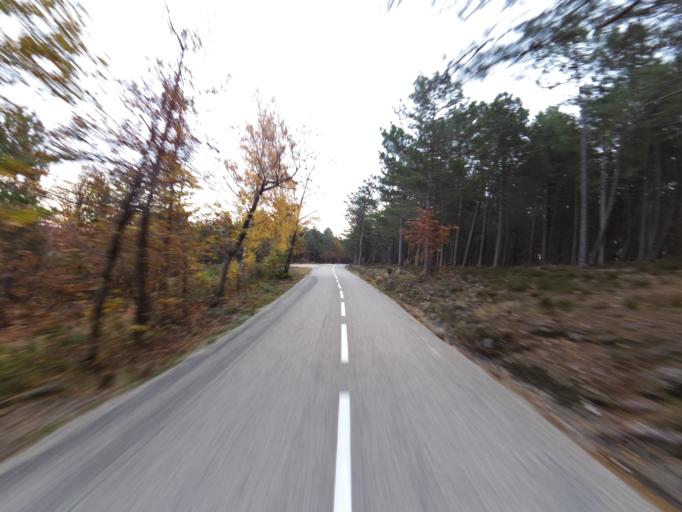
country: FR
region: Rhone-Alpes
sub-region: Departement de l'Ardeche
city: Lablachere
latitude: 44.4948
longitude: 4.1338
